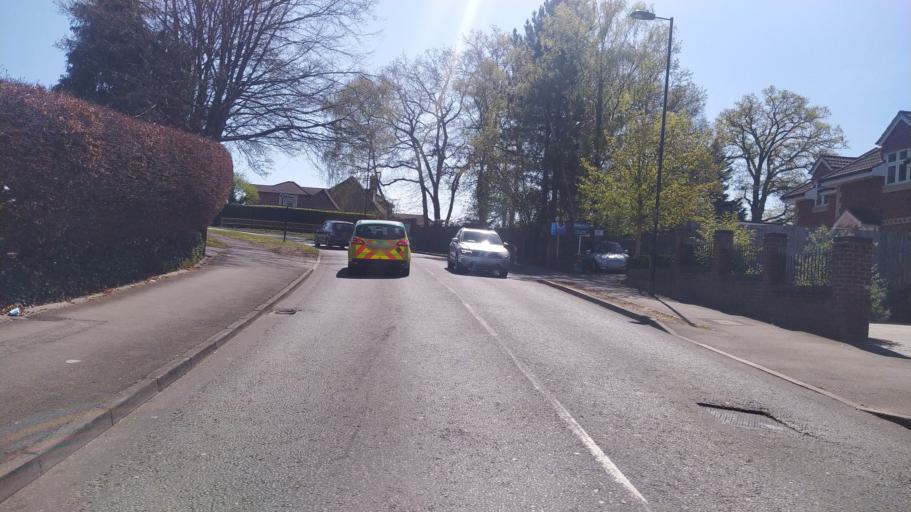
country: GB
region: England
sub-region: Southampton
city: Southampton
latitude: 50.9360
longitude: -1.4207
